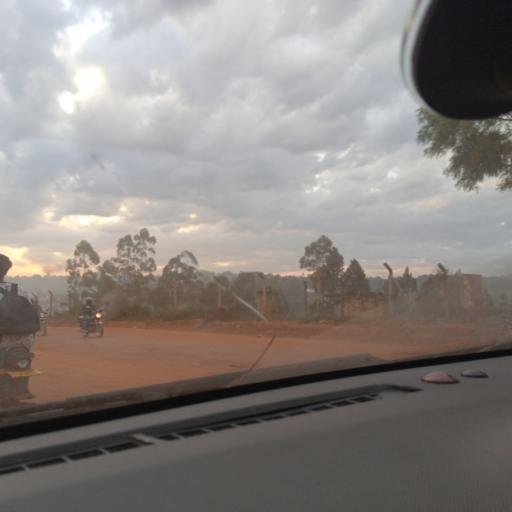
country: UG
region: Central Region
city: Masaka
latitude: -0.3327
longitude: 31.7443
